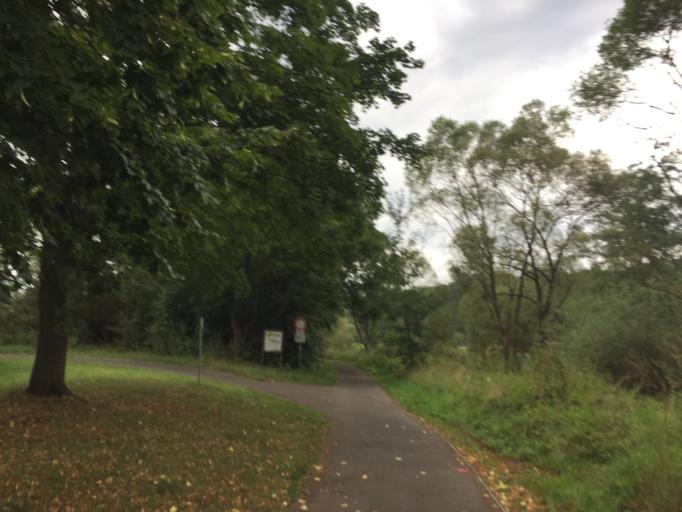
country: DE
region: Hesse
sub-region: Regierungsbezirk Kassel
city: Rotenburg an der Fulda
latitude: 50.9891
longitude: 9.7586
